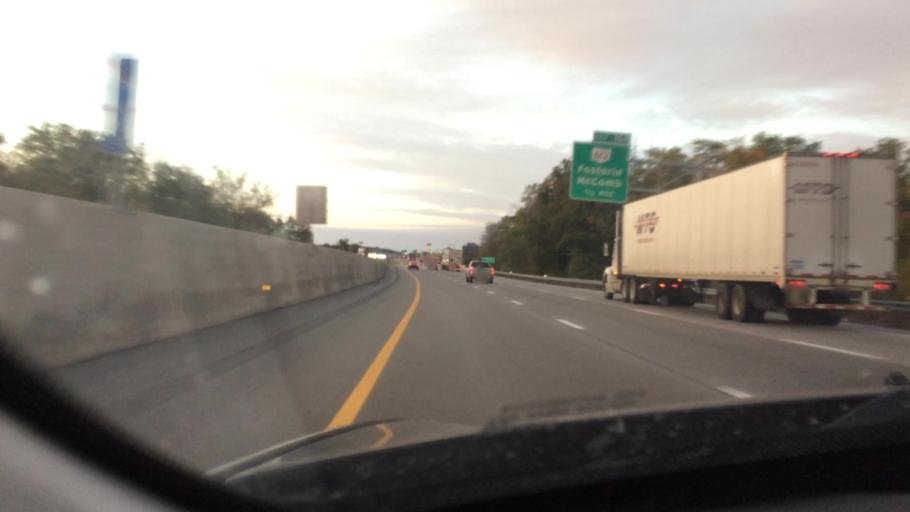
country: US
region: Ohio
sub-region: Wood County
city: North Baltimore
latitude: 41.1488
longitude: -83.6589
